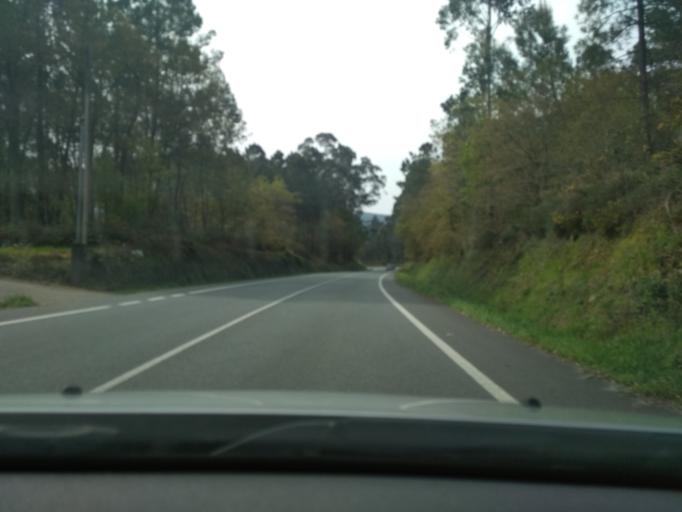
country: ES
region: Galicia
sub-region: Provincia de Pontevedra
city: Catoira
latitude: 42.6657
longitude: -8.7038
